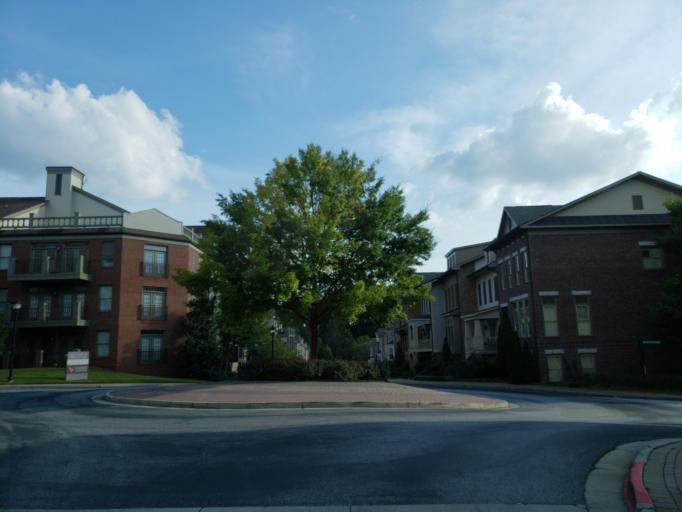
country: US
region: Georgia
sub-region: Cobb County
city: Vinings
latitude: 33.8427
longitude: -84.4913
